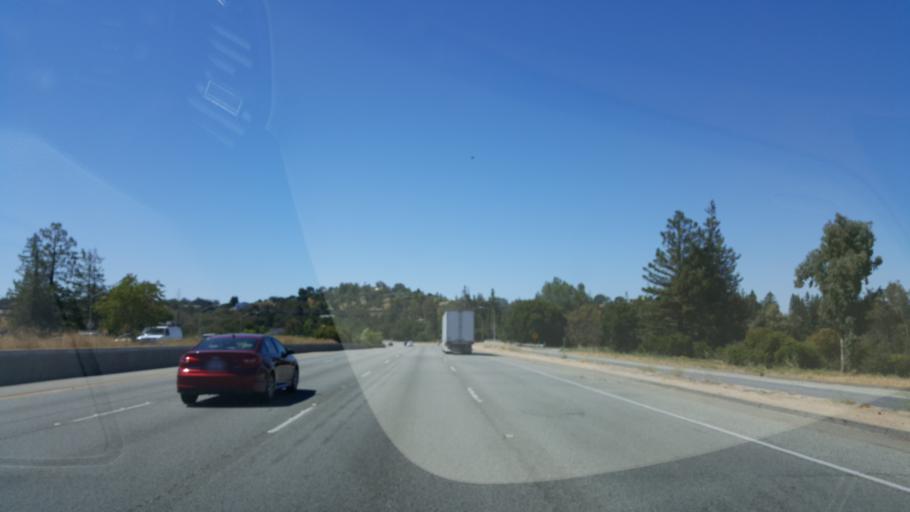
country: US
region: California
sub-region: Santa Clara County
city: Loyola
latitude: 37.3599
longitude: -122.1191
